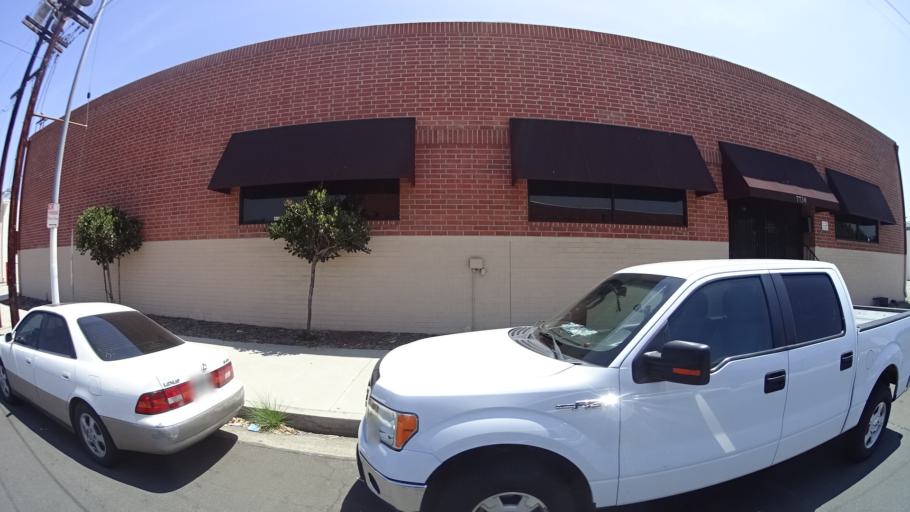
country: US
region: California
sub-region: Los Angeles County
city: Van Nuys
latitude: 34.2111
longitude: -118.4593
